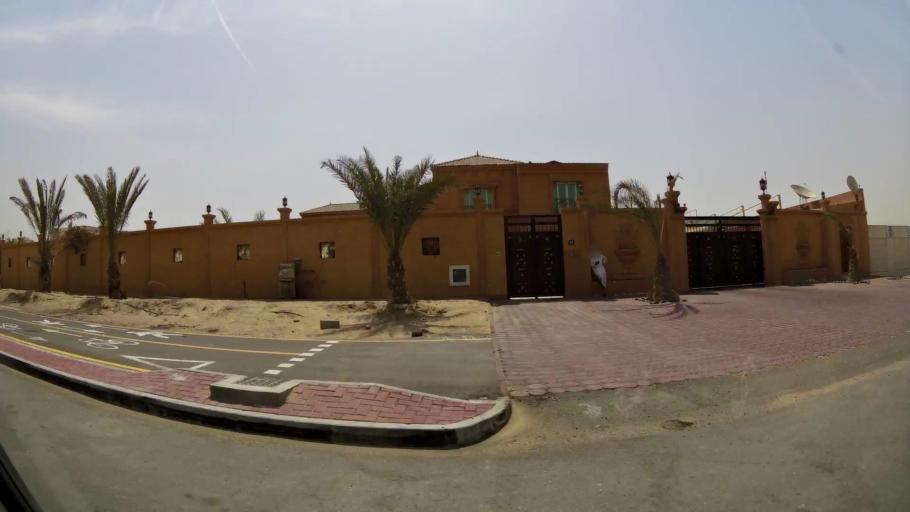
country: AE
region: Ash Shariqah
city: Sharjah
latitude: 25.2593
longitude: 55.4772
